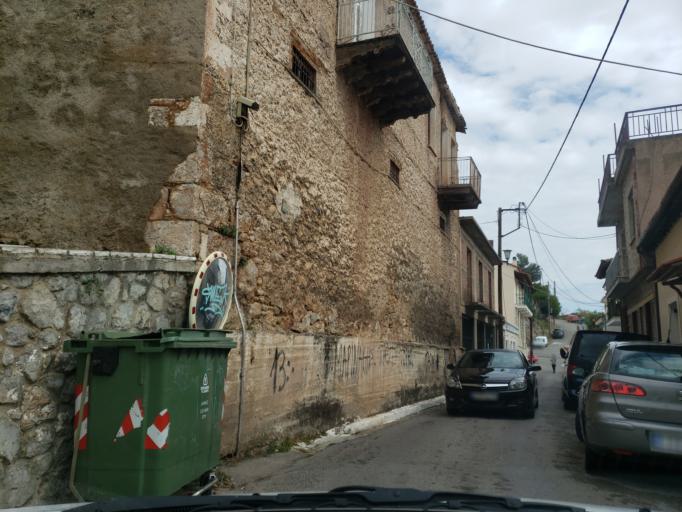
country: GR
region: Central Greece
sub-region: Nomos Fokidos
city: Delphi
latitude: 38.4793
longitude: 22.4958
